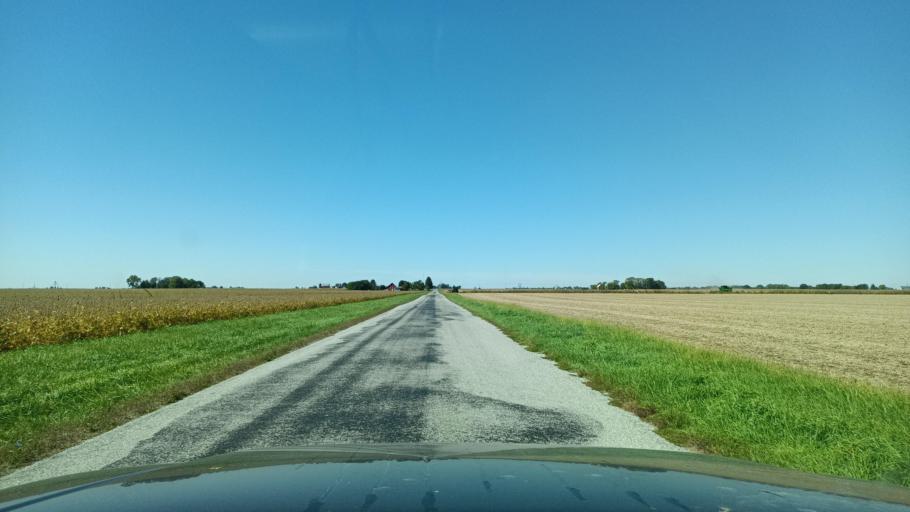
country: US
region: Illinois
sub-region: Champaign County
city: Mahomet
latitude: 40.0988
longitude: -88.3554
